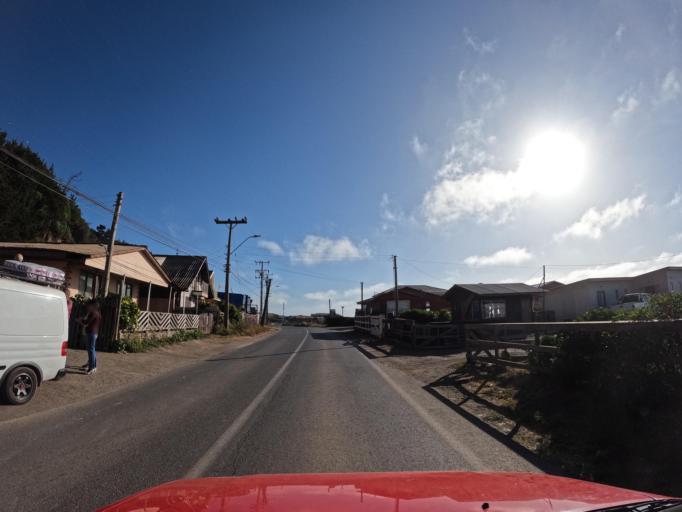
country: CL
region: Maule
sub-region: Provincia de Talca
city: Constitucion
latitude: -34.8928
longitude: -72.1768
